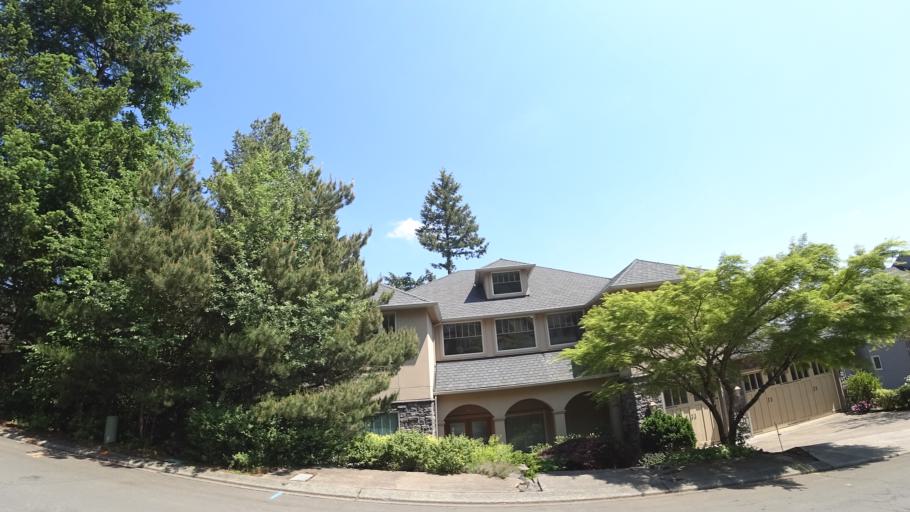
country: US
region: Oregon
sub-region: Washington County
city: Metzger
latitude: 45.4379
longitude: -122.7201
